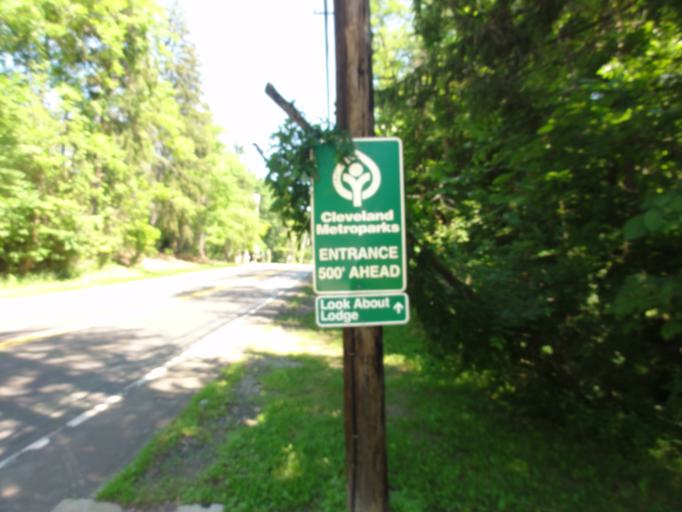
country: US
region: Ohio
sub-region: Cuyahoga County
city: Solon
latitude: 41.3977
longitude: -81.4382
